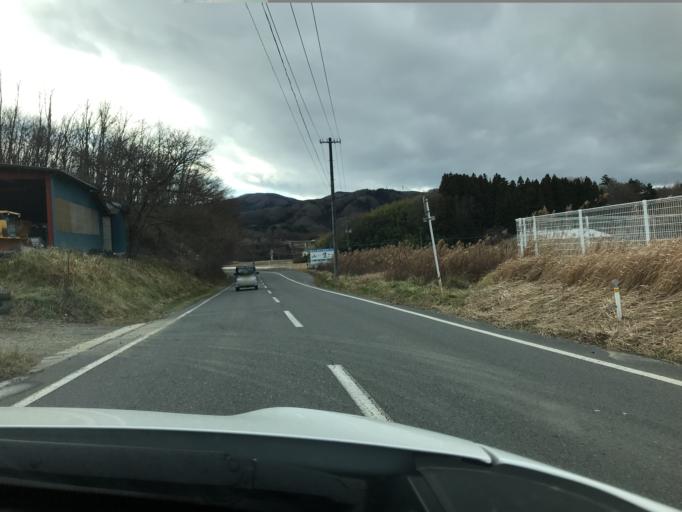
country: JP
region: Fukushima
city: Funehikimachi-funehiki
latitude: 37.3978
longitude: 140.5927
